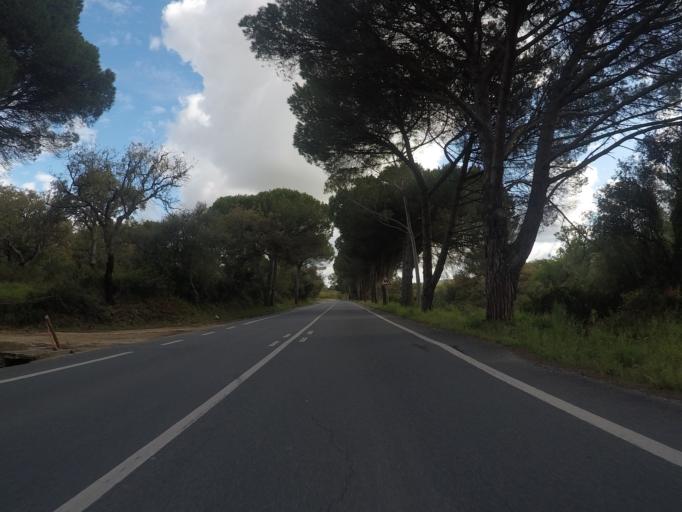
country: PT
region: Faro
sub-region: Aljezur
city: Aljezur
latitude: 37.2799
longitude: -8.8024
